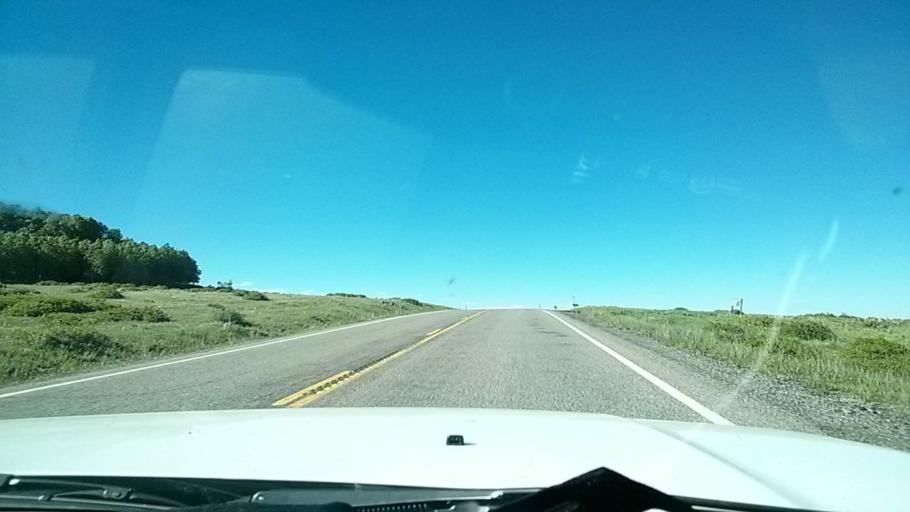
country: US
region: Utah
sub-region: Wayne County
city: Loa
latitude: 38.0401
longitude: -111.3287
